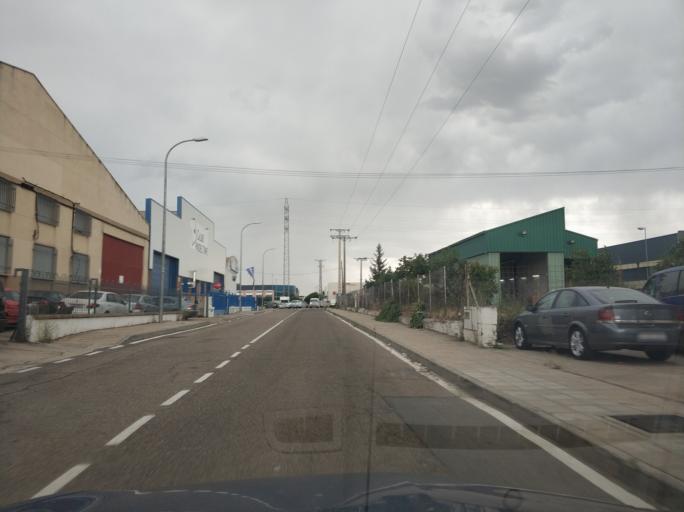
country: ES
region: Castille and Leon
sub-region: Provincia de Salamanca
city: Carbajosa de la Sagrada
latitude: 40.9438
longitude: -5.6588
